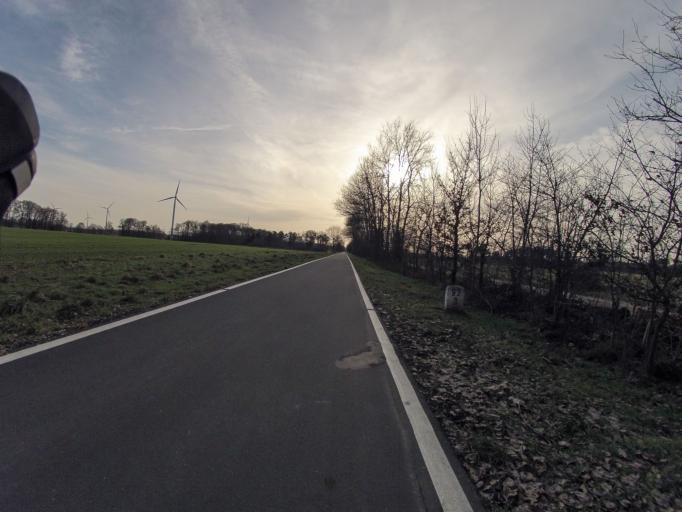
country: DE
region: North Rhine-Westphalia
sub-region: Regierungsbezirk Munster
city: Neuenkirchen
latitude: 52.1940
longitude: 7.3840
